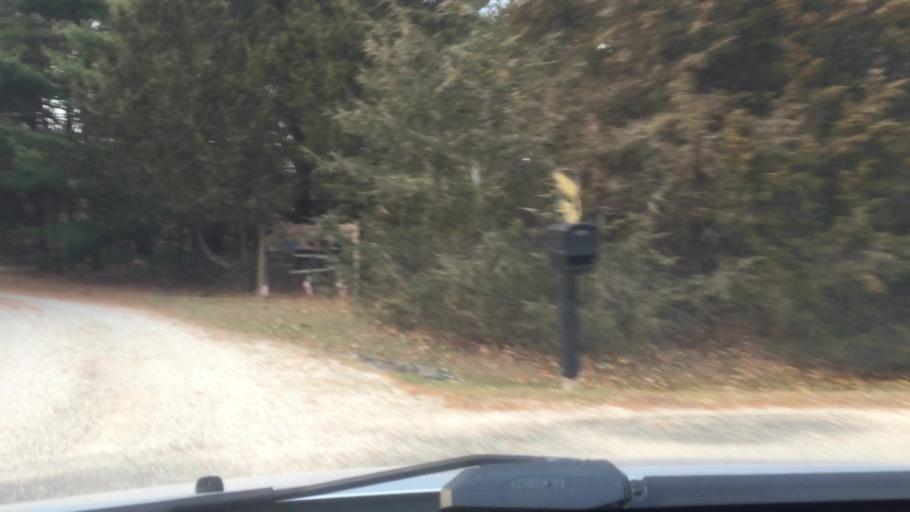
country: US
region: Wisconsin
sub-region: Waukesha County
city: North Prairie
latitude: 42.9329
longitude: -88.4511
